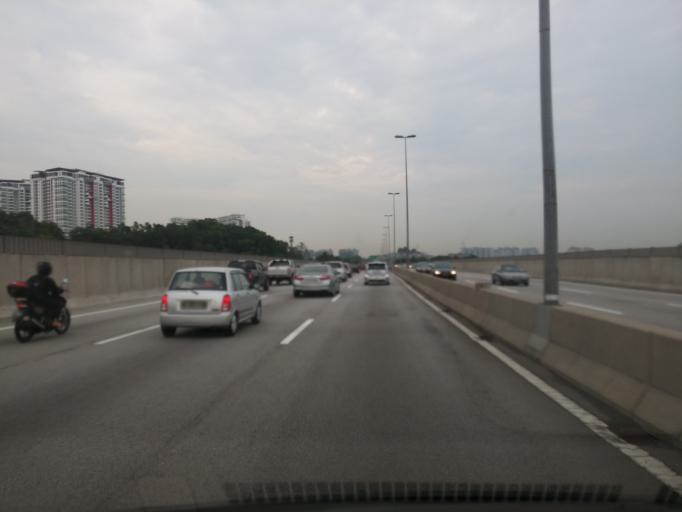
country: MY
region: Kuala Lumpur
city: Kuala Lumpur
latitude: 3.0708
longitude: 101.6861
